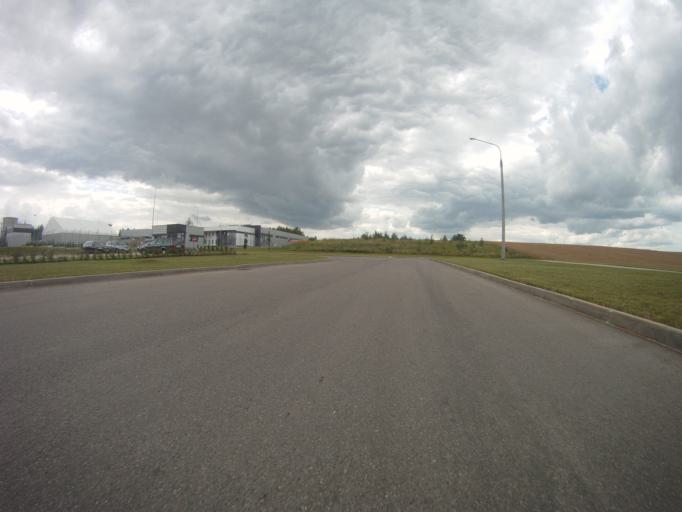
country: BY
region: Minsk
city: Azyartso
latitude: 53.8763
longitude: 27.3988
